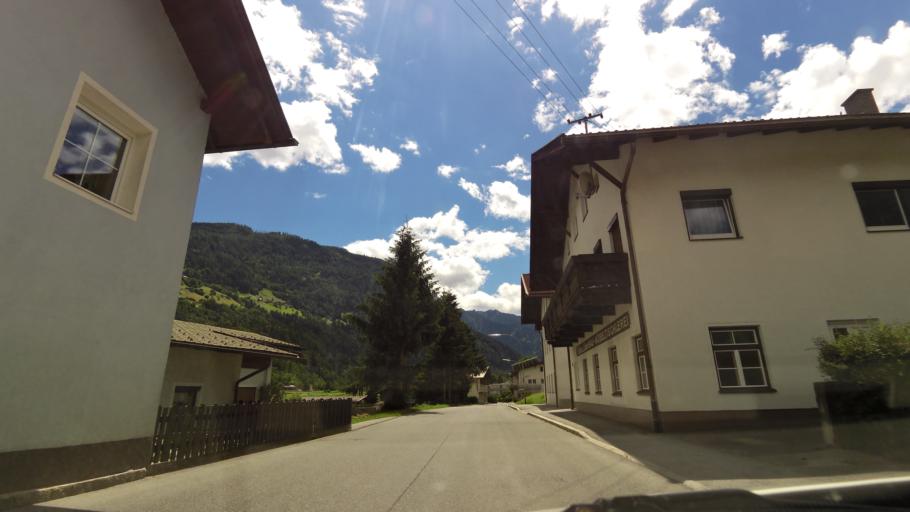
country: AT
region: Tyrol
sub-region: Politischer Bezirk Imst
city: Haiming
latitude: 47.2515
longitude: 10.8849
